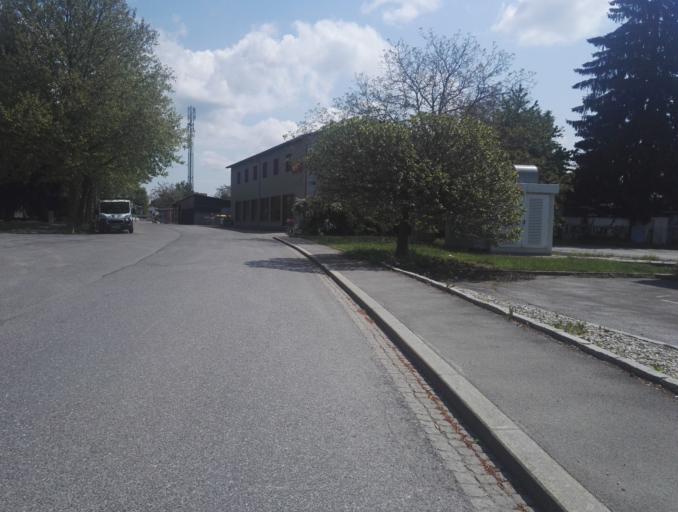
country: AT
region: Styria
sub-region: Politischer Bezirk Graz-Umgebung
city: Feldkirchen bei Graz
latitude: 47.0369
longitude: 15.4630
